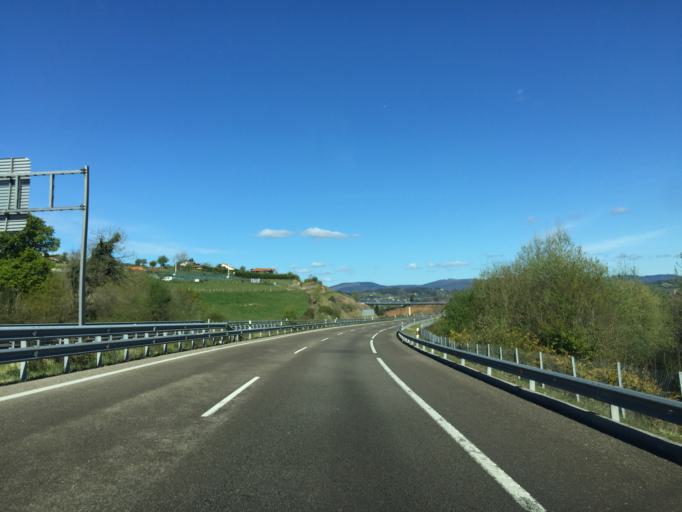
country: ES
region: Asturias
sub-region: Province of Asturias
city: Oviedo
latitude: 43.3491
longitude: -5.9065
